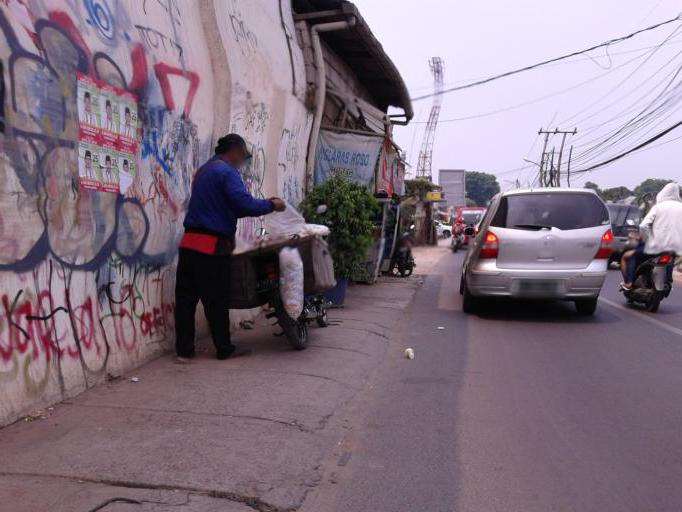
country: ID
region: Banten
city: South Tangerang
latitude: -6.2926
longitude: 106.7584
